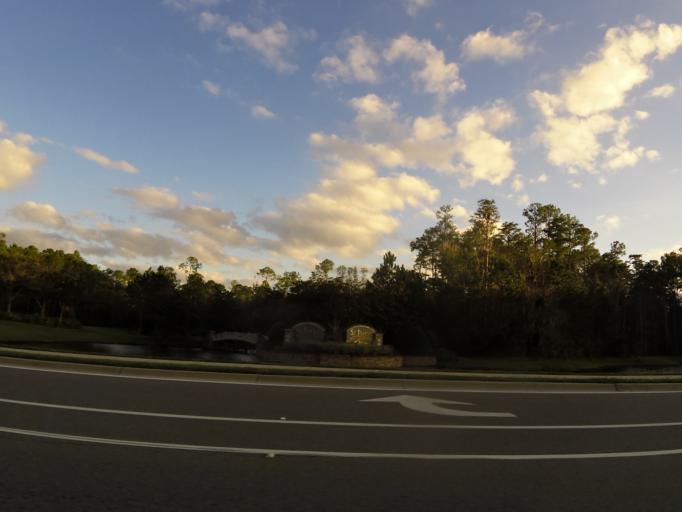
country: US
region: Florida
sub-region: Saint Johns County
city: Fruit Cove
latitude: 30.0601
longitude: -81.5107
